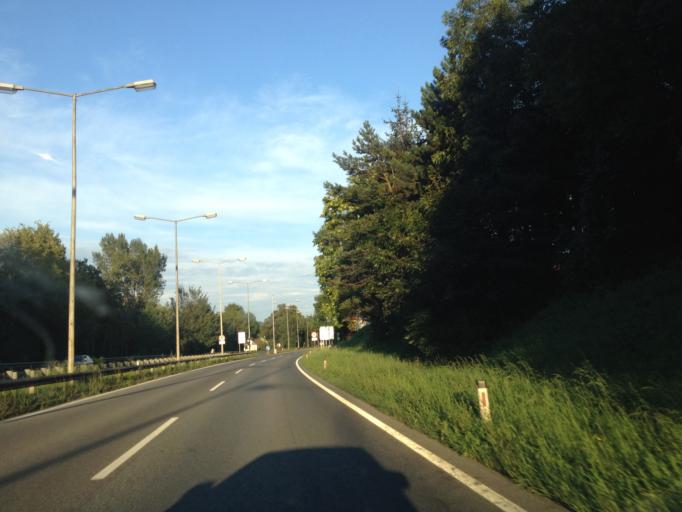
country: AT
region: Styria
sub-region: Graz Stadt
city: Goesting
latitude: 47.1069
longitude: 15.3921
